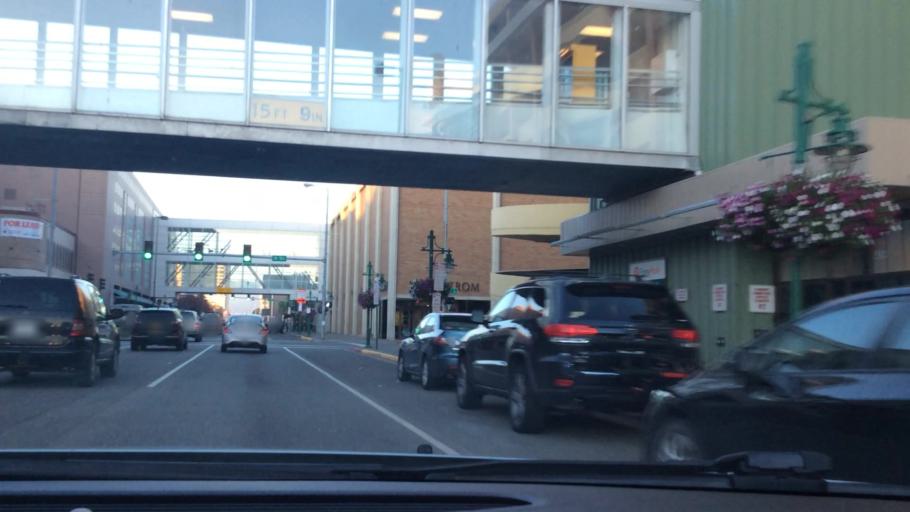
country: US
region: Alaska
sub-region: Anchorage Municipality
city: Anchorage
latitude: 61.2166
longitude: -149.8904
